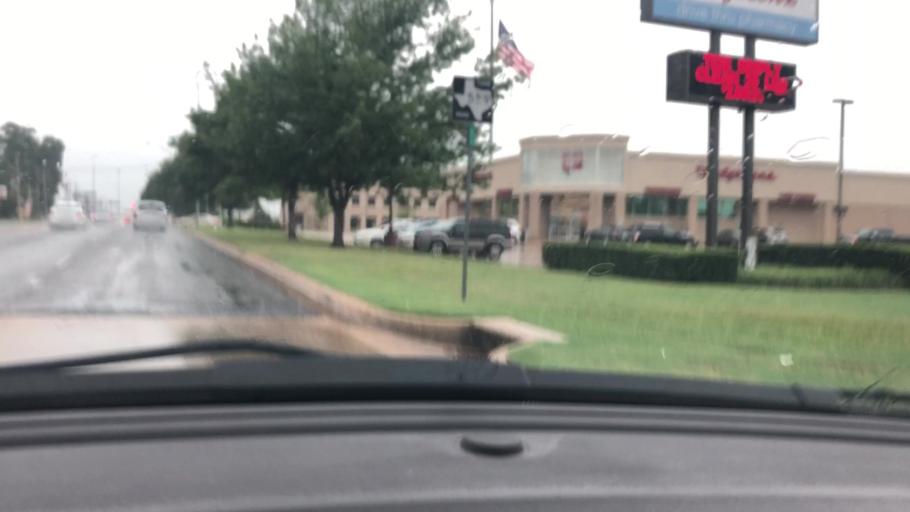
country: US
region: Texas
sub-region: Bowie County
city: Wake Village
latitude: 33.4522
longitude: -94.0803
